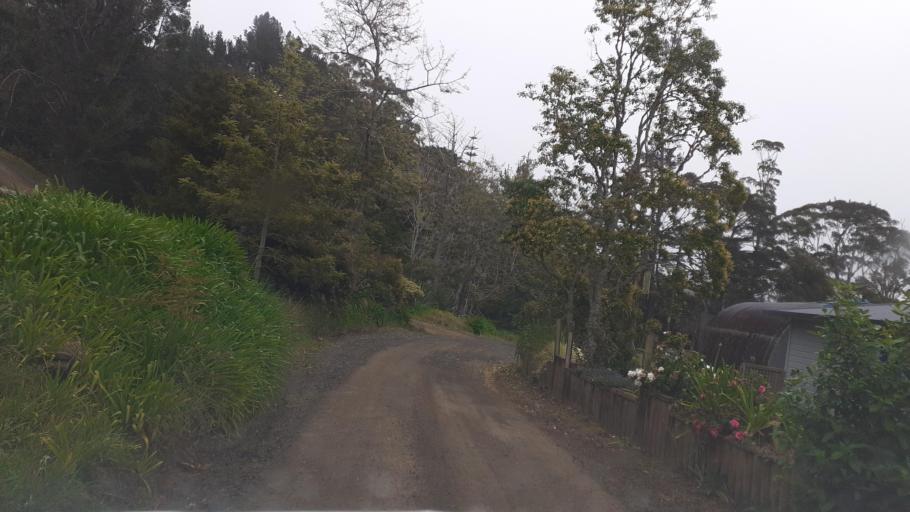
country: NZ
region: Northland
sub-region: Far North District
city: Kerikeri
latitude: -35.1035
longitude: 173.9261
